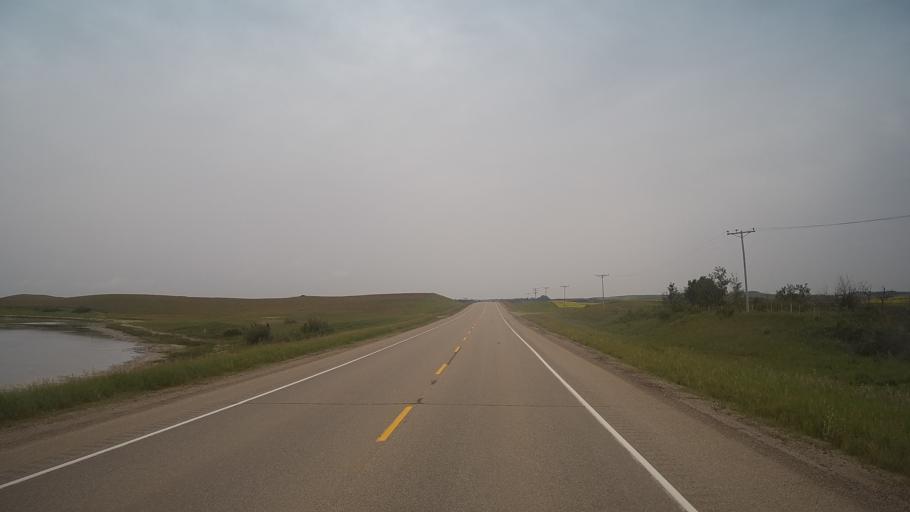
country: CA
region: Saskatchewan
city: Biggar
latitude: 52.0565
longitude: -107.8220
